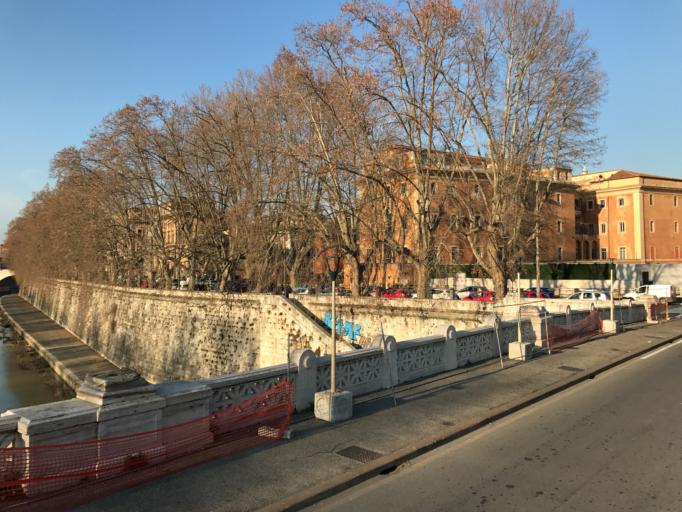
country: VA
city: Vatican City
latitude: 41.8961
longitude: 12.4661
